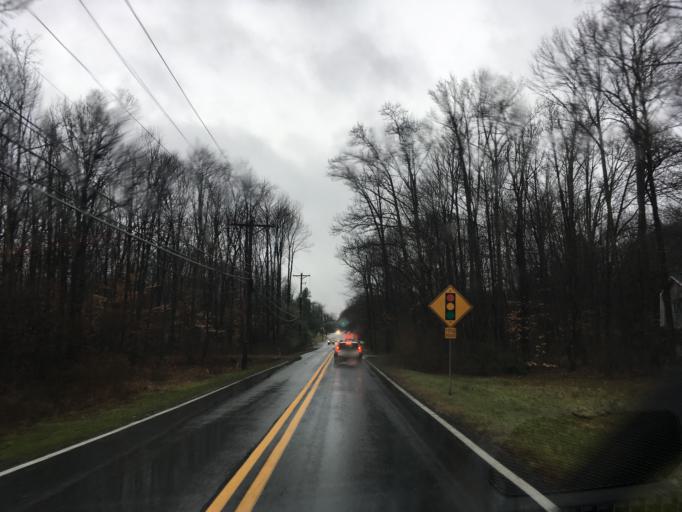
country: US
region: Delaware
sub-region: New Castle County
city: Claymont
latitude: 39.8158
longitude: -75.5037
